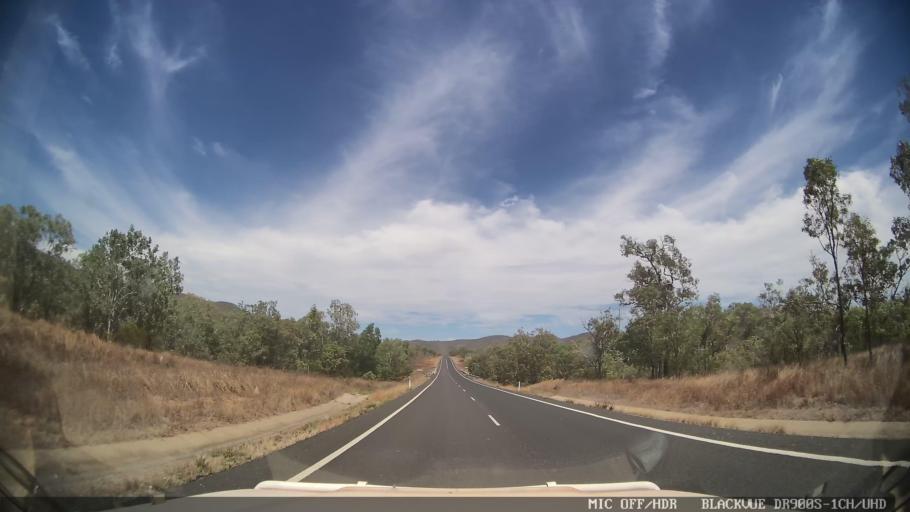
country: AU
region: Queensland
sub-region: Cook
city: Cooktown
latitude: -15.9359
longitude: 144.8386
